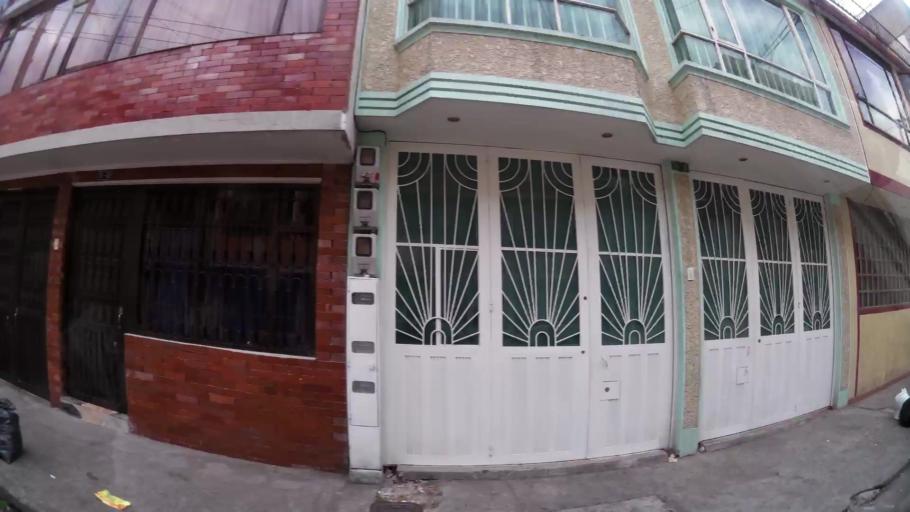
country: CO
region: Cundinamarca
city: Funza
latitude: 4.7057
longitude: -74.1257
